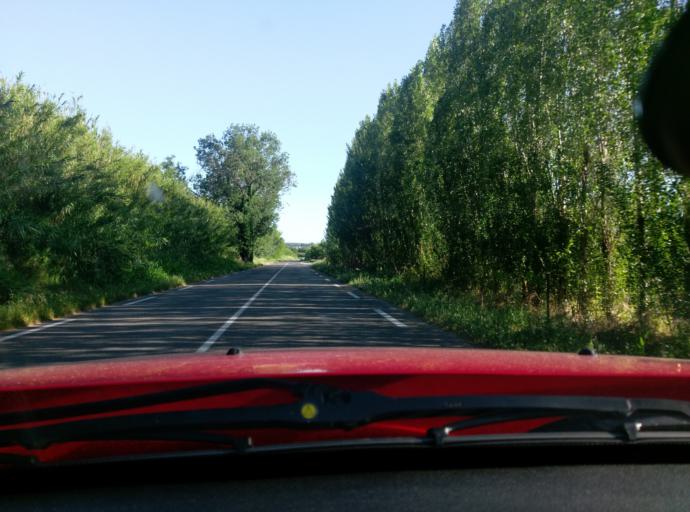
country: FR
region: Languedoc-Roussillon
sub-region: Departement du Gard
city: Remoulins
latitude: 43.9461
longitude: 4.5600
